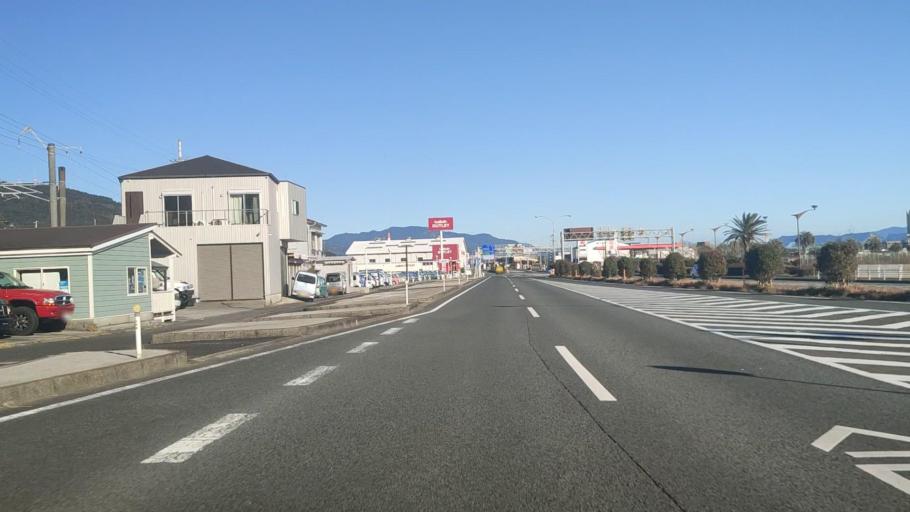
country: JP
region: Miyazaki
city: Nobeoka
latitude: 32.5406
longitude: 131.6784
